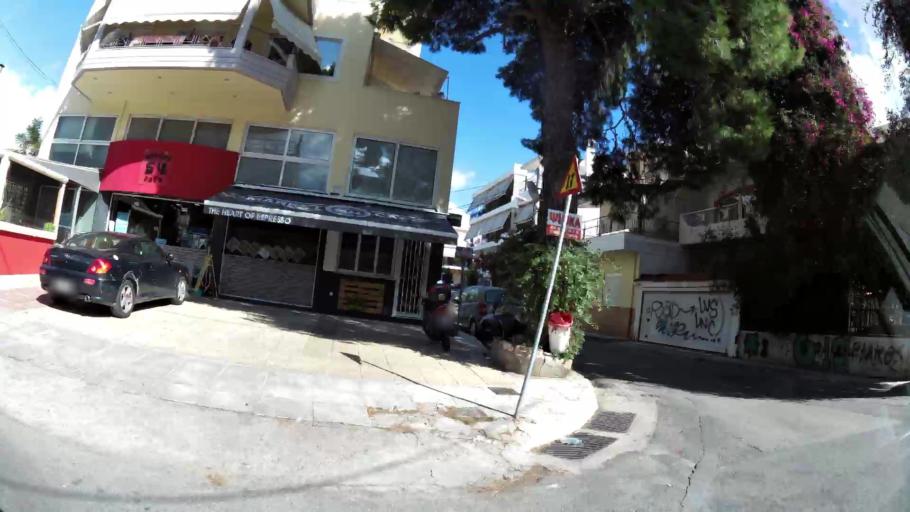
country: GR
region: Attica
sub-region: Nomarchia Athinas
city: Neo Psychiko
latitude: 38.0080
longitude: 23.7913
